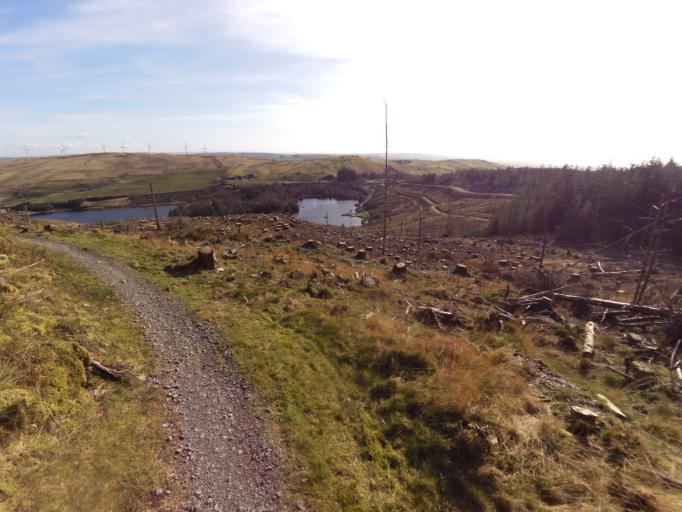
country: GB
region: Wales
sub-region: County of Ceredigion
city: Bow Street
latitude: 52.4208
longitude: -3.8814
